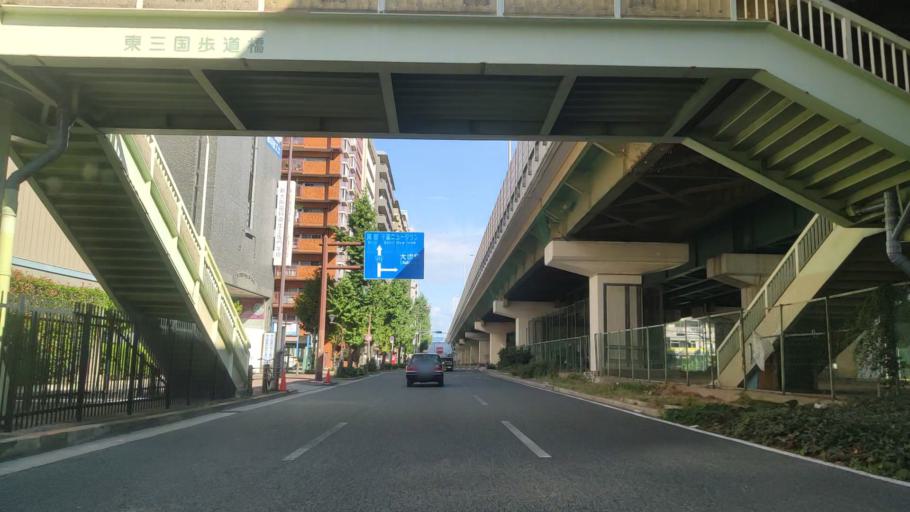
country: JP
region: Osaka
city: Suita
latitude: 34.7433
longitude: 135.4980
